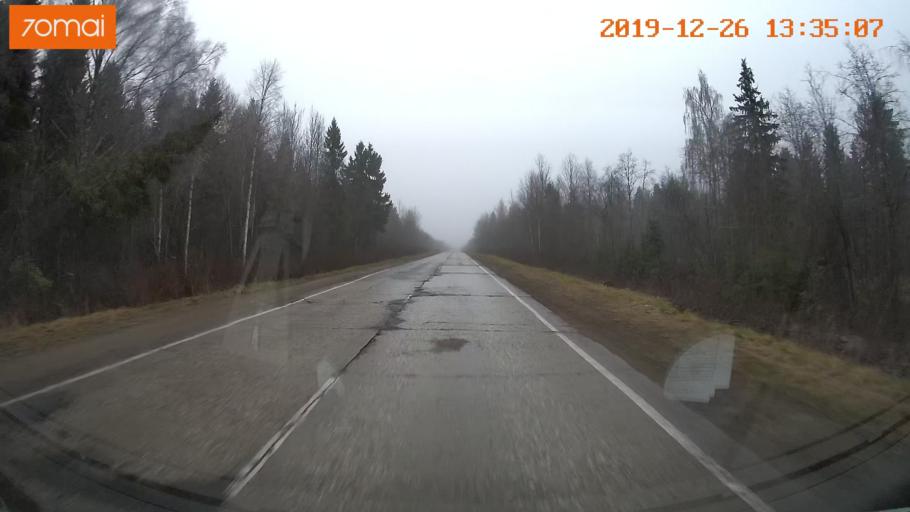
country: RU
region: Vologda
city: Sheksna
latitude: 58.7974
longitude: 38.3349
